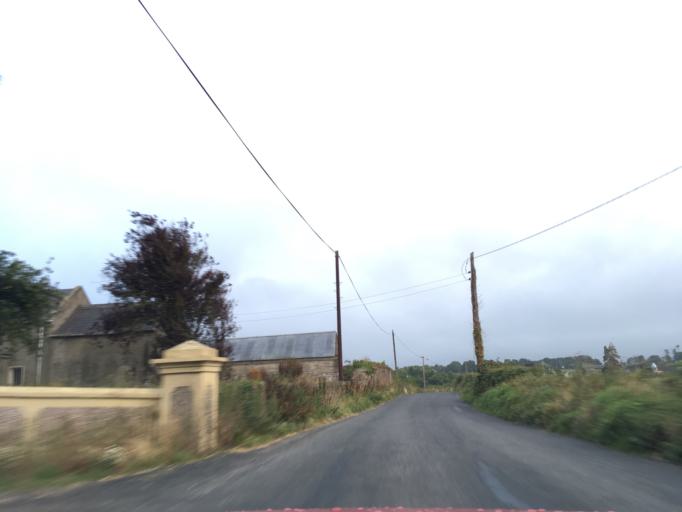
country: IE
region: Munster
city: Cashel
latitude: 52.4785
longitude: -7.9792
